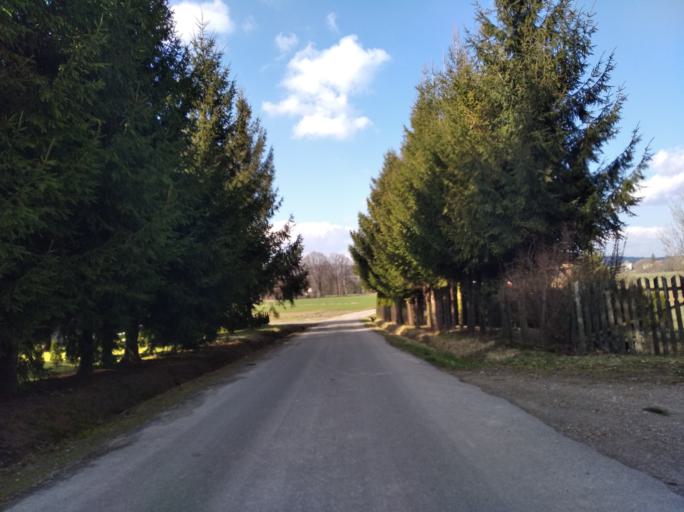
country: PL
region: Subcarpathian Voivodeship
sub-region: Powiat strzyzowski
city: Wysoka Strzyzowska
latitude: 49.8557
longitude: 21.7092
